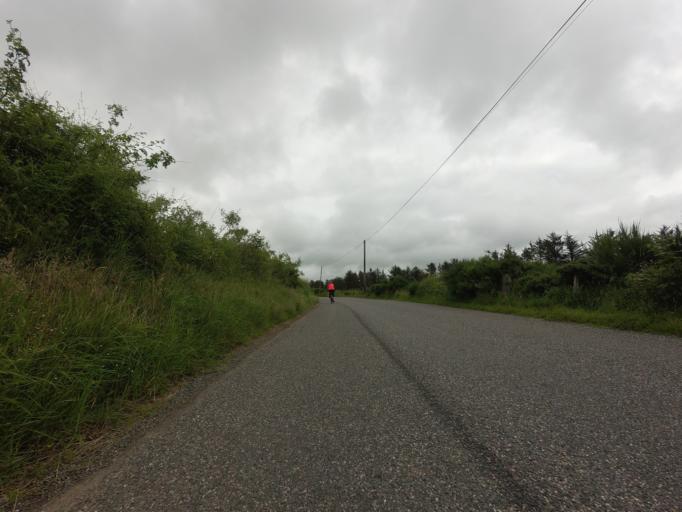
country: GB
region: Scotland
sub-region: Aberdeenshire
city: Turriff
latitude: 57.5353
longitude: -2.3743
